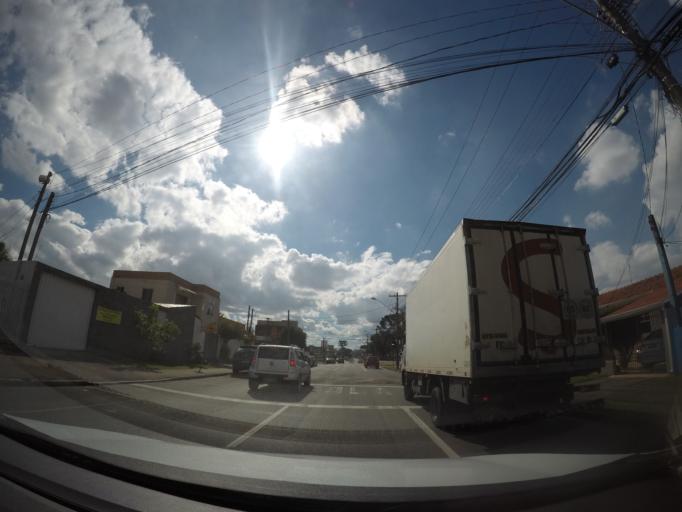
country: BR
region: Parana
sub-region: Curitiba
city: Curitiba
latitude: -25.4815
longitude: -49.2541
